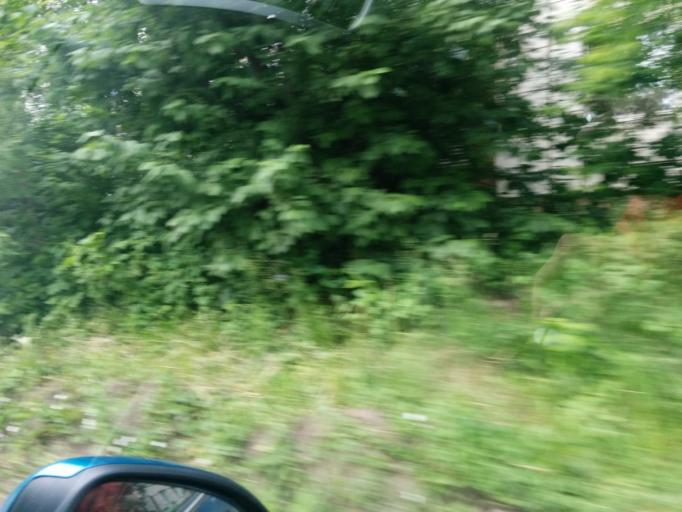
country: RU
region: Perm
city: Kondratovo
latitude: 58.0018
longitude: 56.1200
